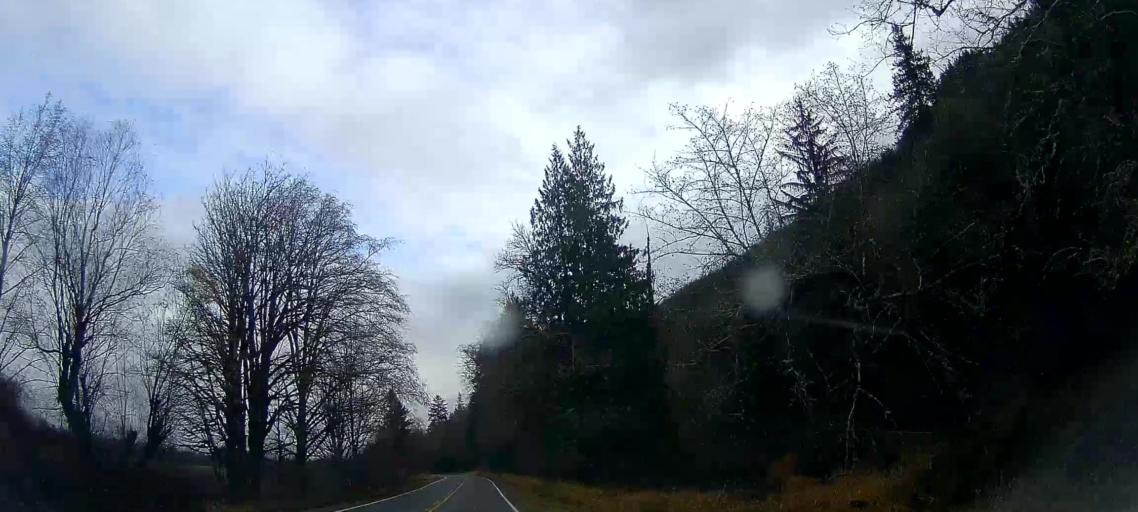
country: US
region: Washington
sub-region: Skagit County
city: Sedro-Woolley
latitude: 48.5157
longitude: -121.9583
